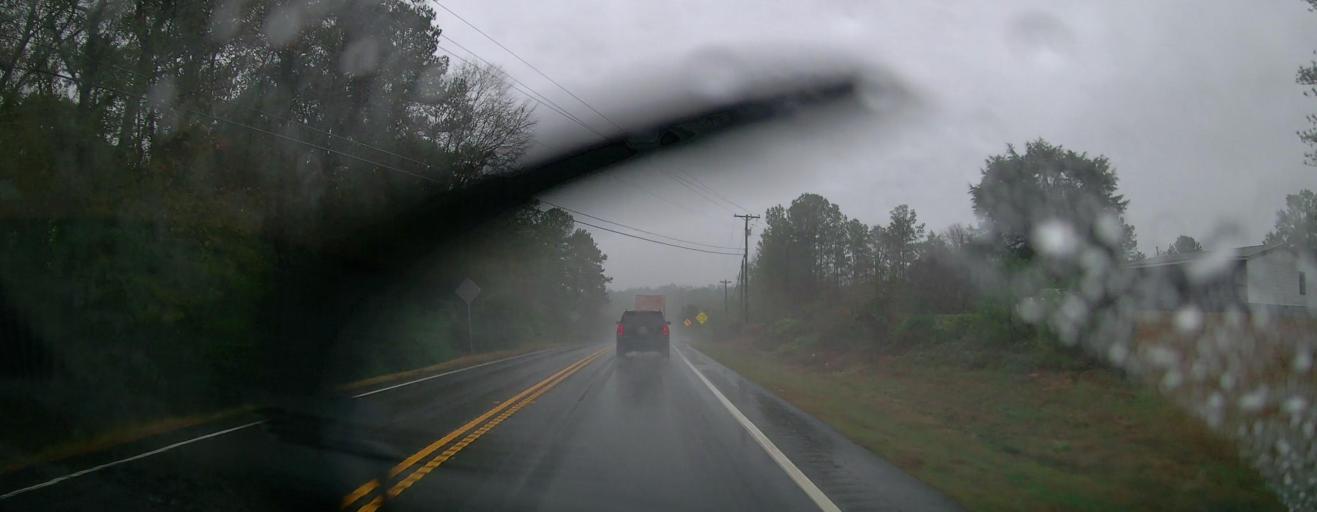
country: US
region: Georgia
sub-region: Putnam County
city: Eatonton
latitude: 33.2245
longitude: -83.4308
